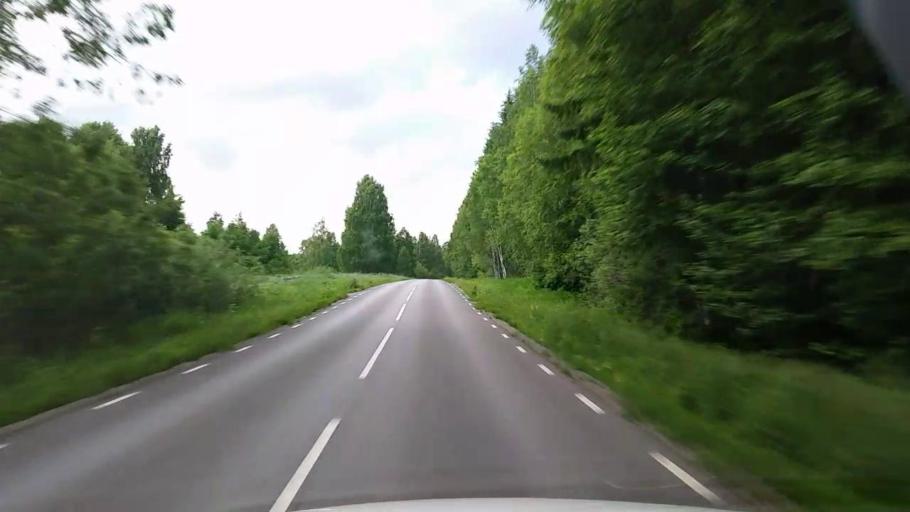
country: SE
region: Vaestmanland
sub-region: Kopings Kommun
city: Kolsva
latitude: 59.7576
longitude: 15.8355
